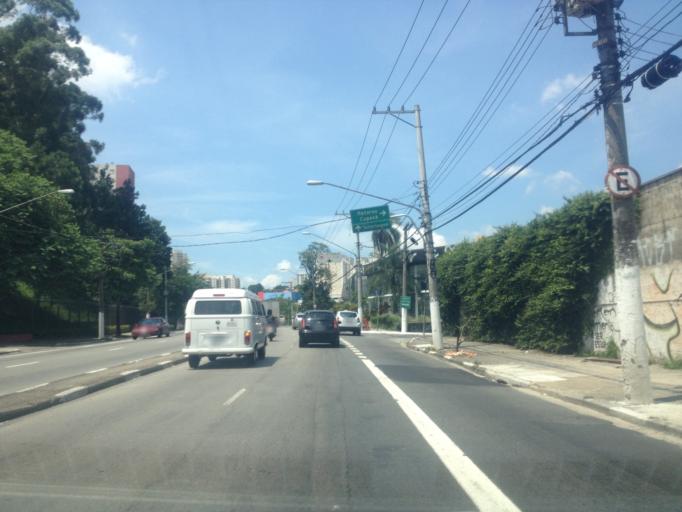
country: BR
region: Sao Paulo
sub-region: Diadema
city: Diadema
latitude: -23.6610
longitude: -46.6795
